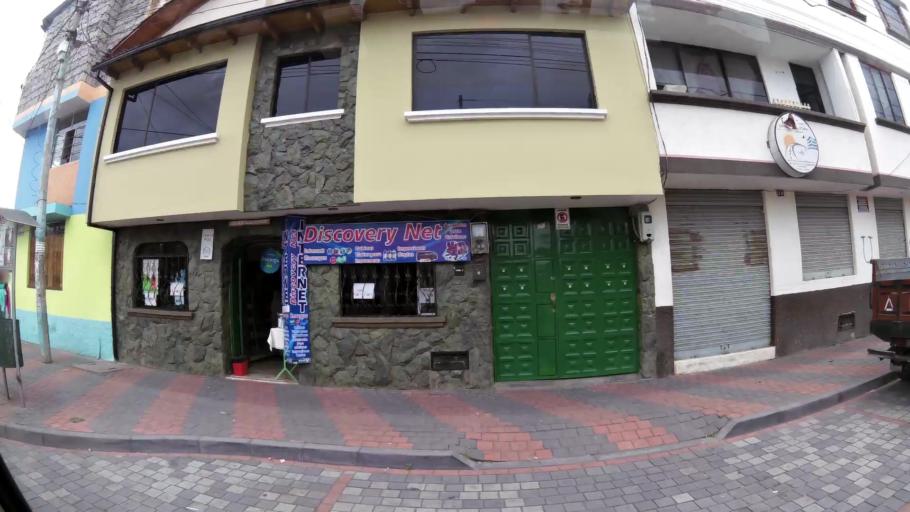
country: EC
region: Cotopaxi
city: San Miguel de Salcedo
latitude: -1.0458
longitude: -78.5902
